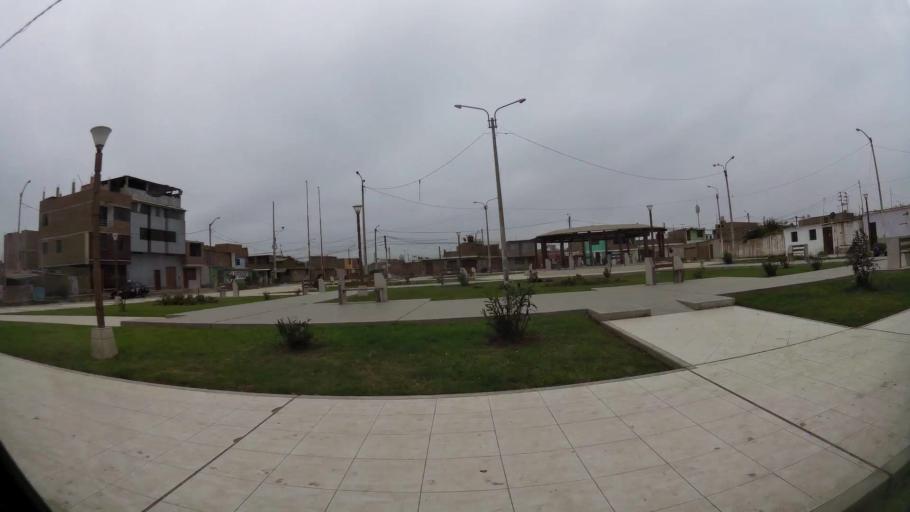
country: PE
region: La Libertad
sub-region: Provincia de Trujillo
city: Buenos Aires
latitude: -8.1489
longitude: -79.0489
